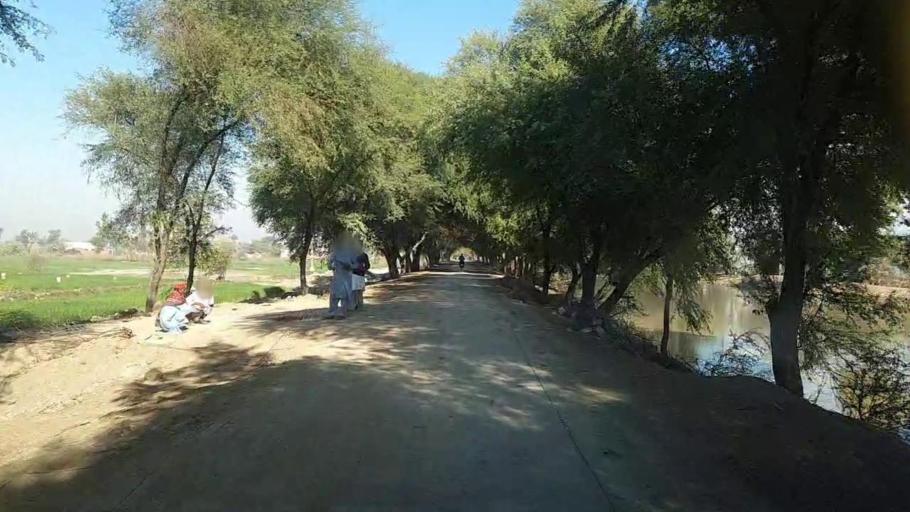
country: PK
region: Sindh
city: Khairpur
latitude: 28.0028
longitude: 69.6517
